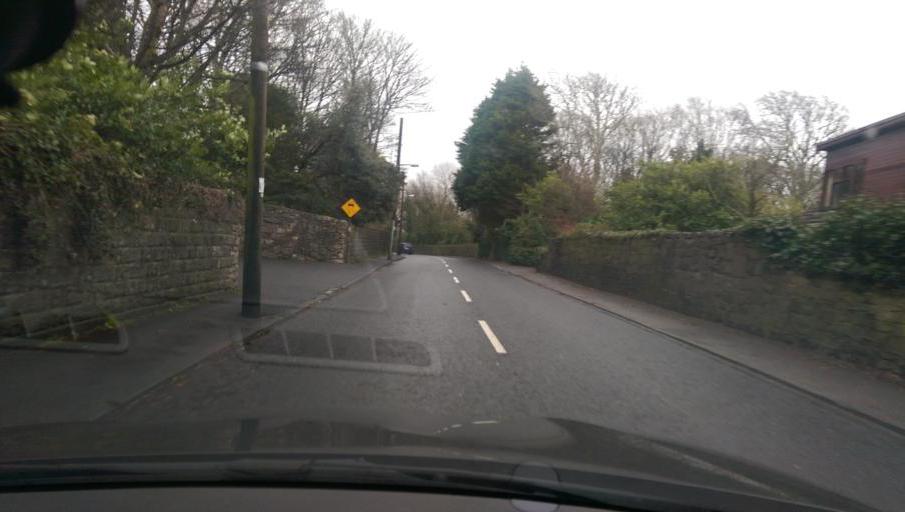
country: IE
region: Connaught
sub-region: County Galway
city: Gaillimh
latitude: 53.2682
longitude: -9.0828
